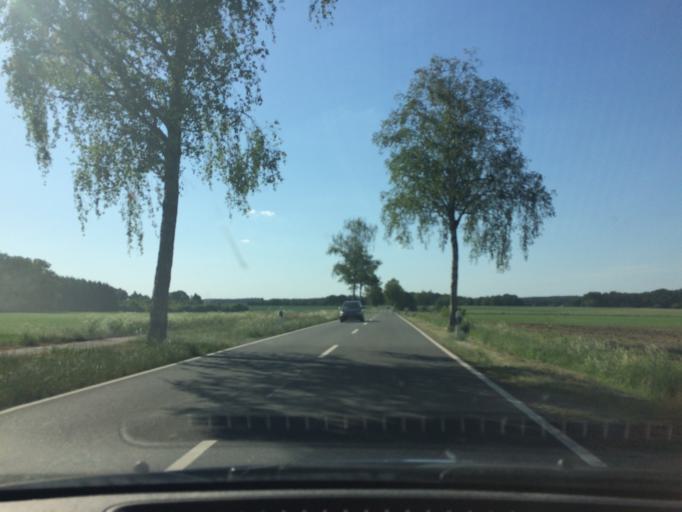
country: DE
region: Lower Saxony
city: Bad Fallingbostel
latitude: 52.9187
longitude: 9.7050
